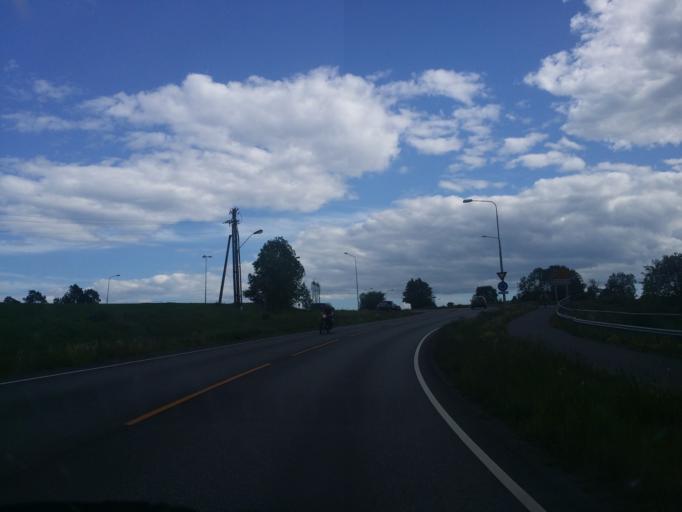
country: NO
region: Akershus
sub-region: Baerum
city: Sandvika
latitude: 59.9300
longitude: 10.5666
